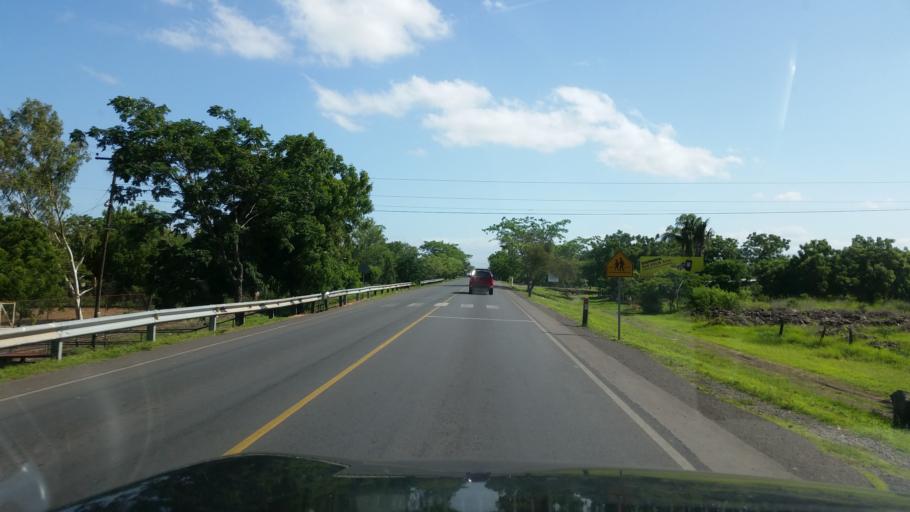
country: NI
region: Matagalpa
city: Ciudad Dario
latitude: 12.7972
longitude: -86.1245
